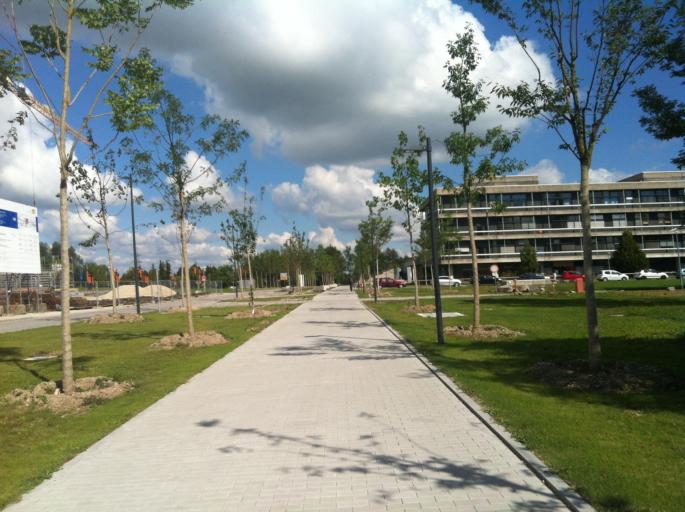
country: DE
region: Bavaria
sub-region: Upper Bavaria
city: Garching bei Munchen
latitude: 48.2676
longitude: 11.6729
